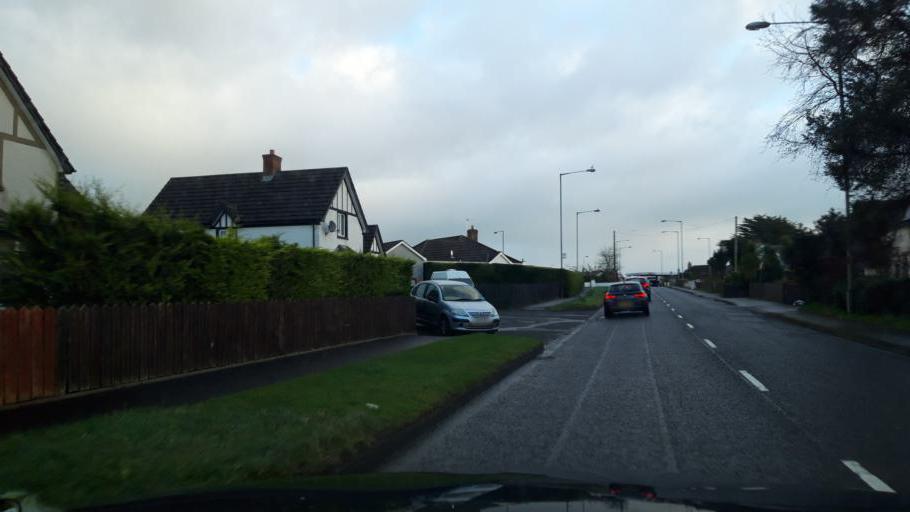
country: GB
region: Northern Ireland
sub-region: Moyle District
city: Ballycastle
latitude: 55.1959
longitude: -6.2642
